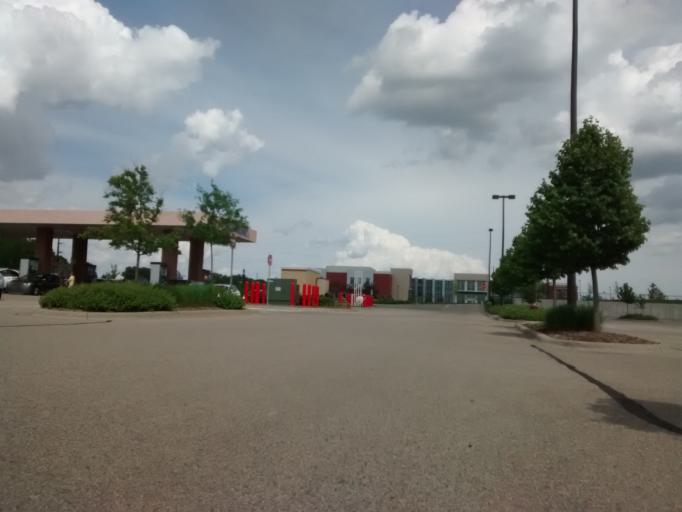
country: US
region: Minnesota
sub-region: Dakota County
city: Burnsville
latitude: 44.7509
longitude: -93.2945
